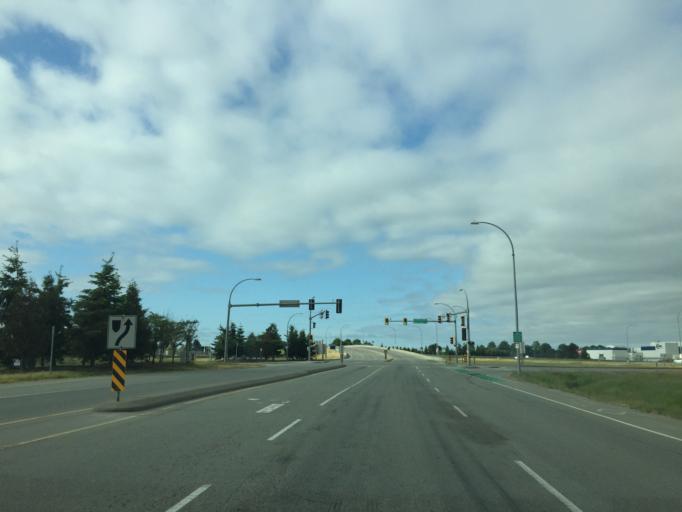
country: CA
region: British Columbia
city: Richmond
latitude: 49.1977
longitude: -123.1497
